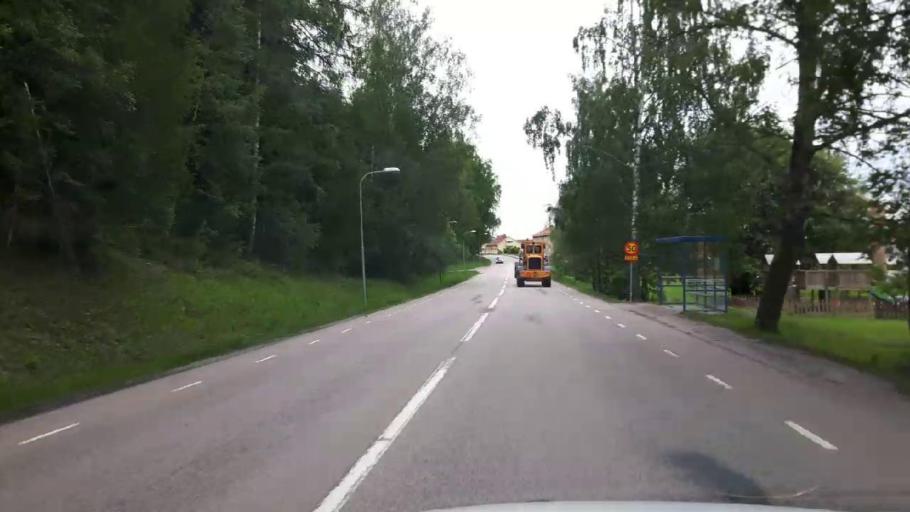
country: SE
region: Vaestmanland
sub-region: Kopings Kommun
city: Kolsva
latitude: 59.6054
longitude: 15.8331
